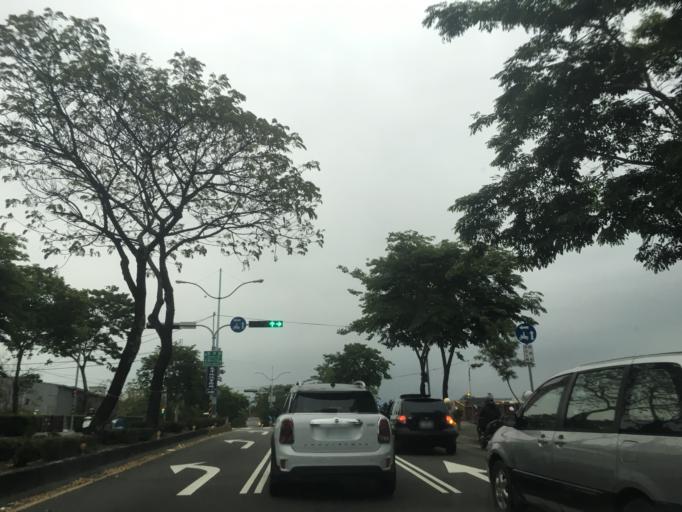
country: TW
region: Taiwan
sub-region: Taichung City
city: Taichung
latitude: 24.1420
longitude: 120.7212
